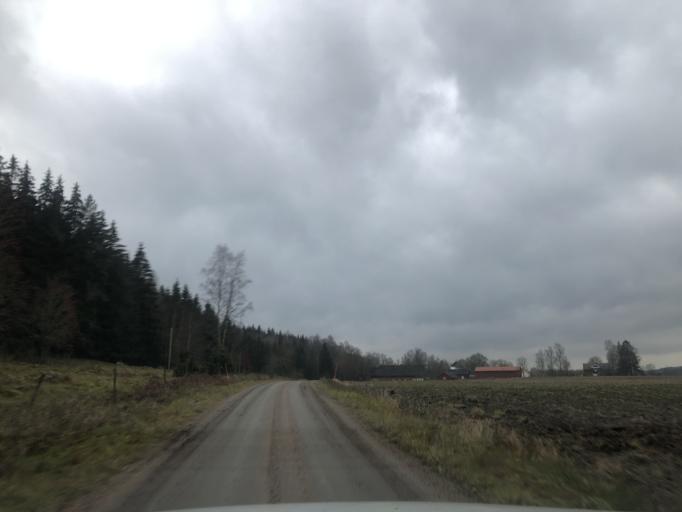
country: SE
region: Vaestra Goetaland
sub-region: Ulricehamns Kommun
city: Ulricehamn
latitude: 57.9034
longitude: 13.4837
